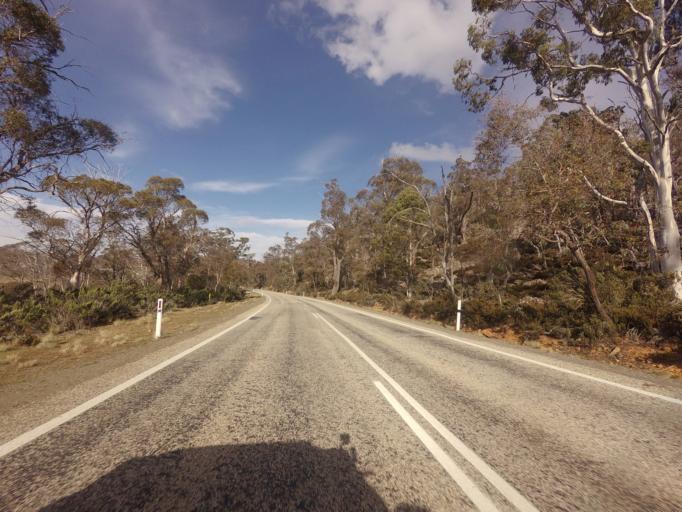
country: AU
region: Tasmania
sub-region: Meander Valley
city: Deloraine
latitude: -41.9892
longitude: 146.6811
